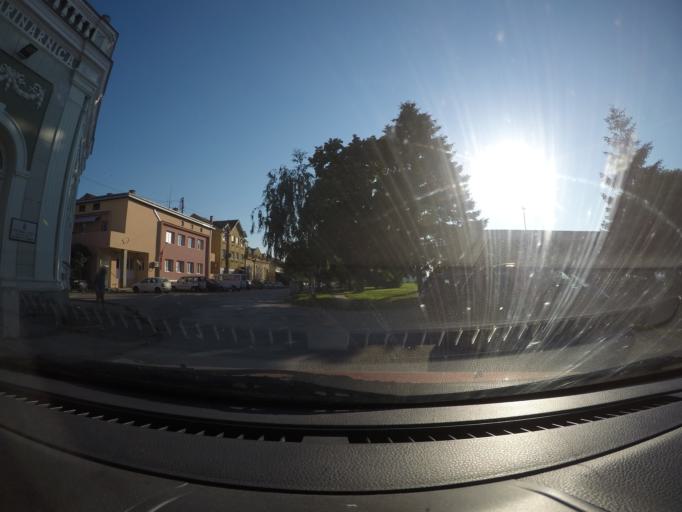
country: RS
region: Central Serbia
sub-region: Branicevski Okrug
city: Veliko Gradiste
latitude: 44.7672
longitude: 21.5167
